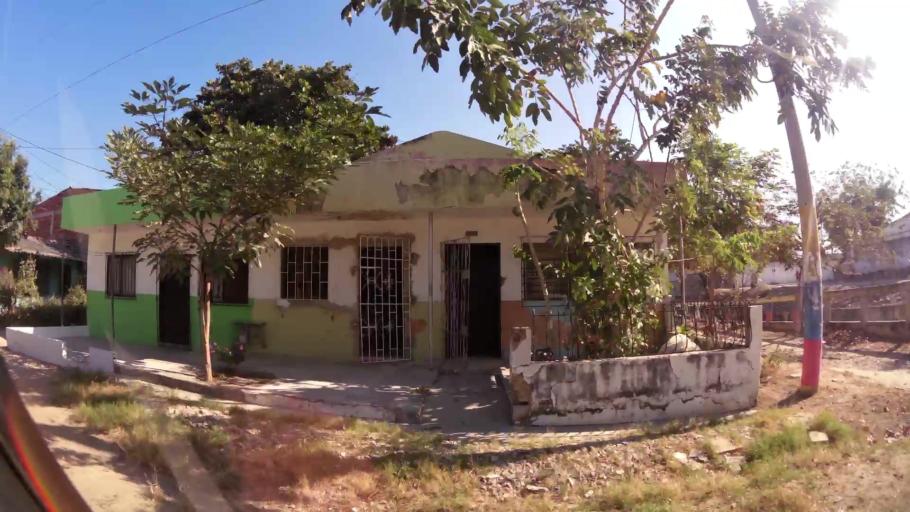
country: CO
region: Atlantico
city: Barranquilla
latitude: 11.0215
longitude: -74.8047
